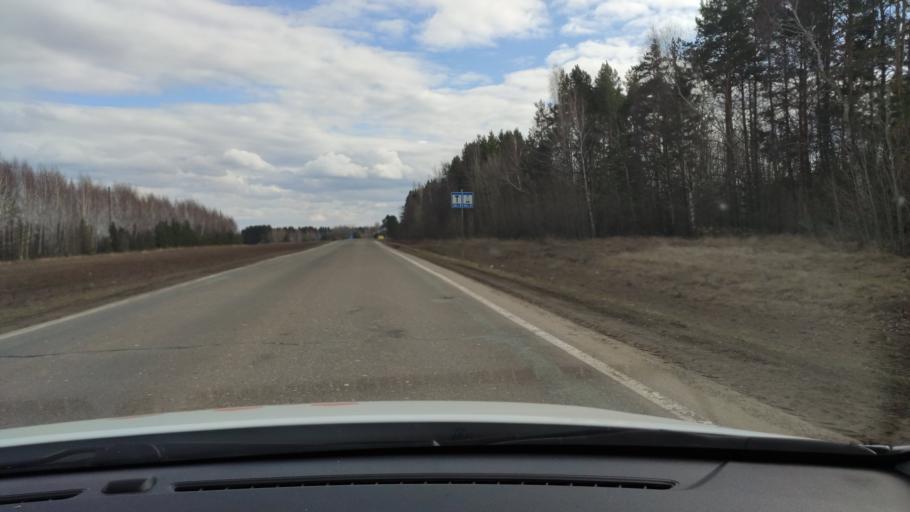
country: RU
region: Tatarstan
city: Vysokaya Gora
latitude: 56.0417
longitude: 49.2213
